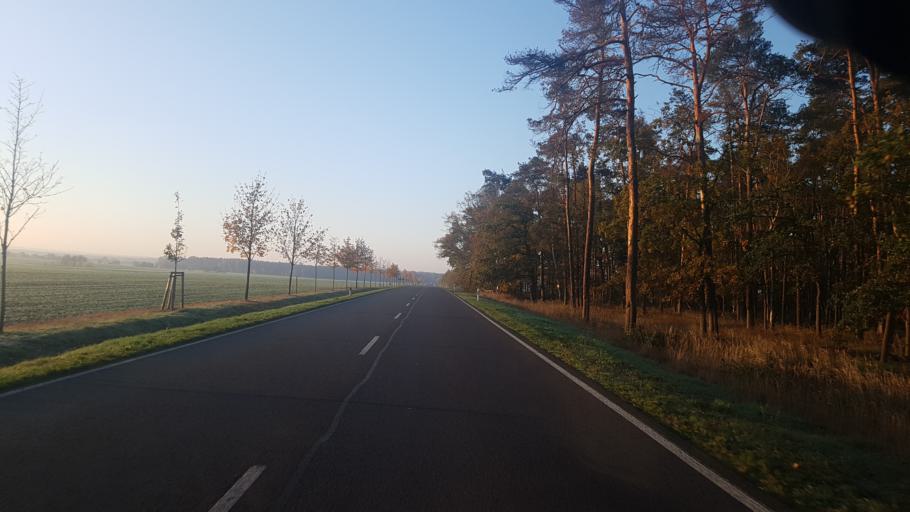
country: DE
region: Saxony
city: Torgau
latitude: 51.4924
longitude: 12.9896
